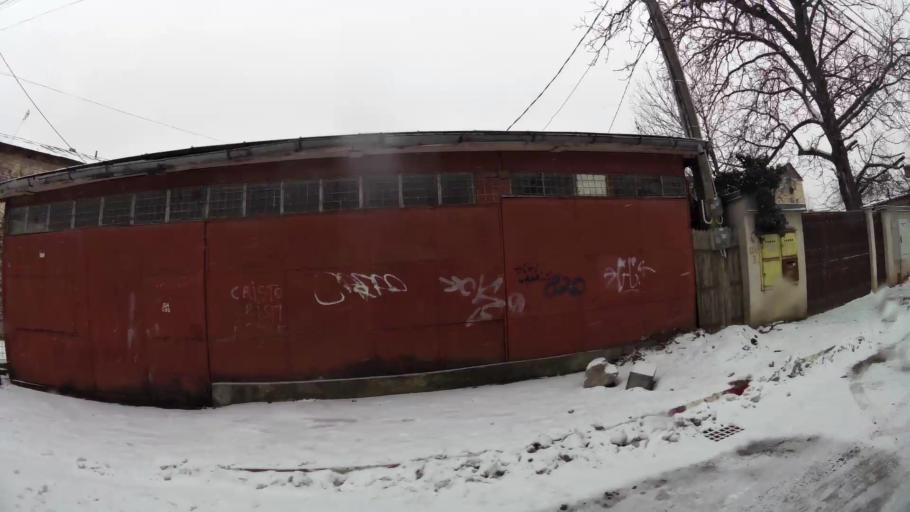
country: RO
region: Dambovita
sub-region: Municipiul Targoviste
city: Targoviste
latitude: 44.9226
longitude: 25.4724
